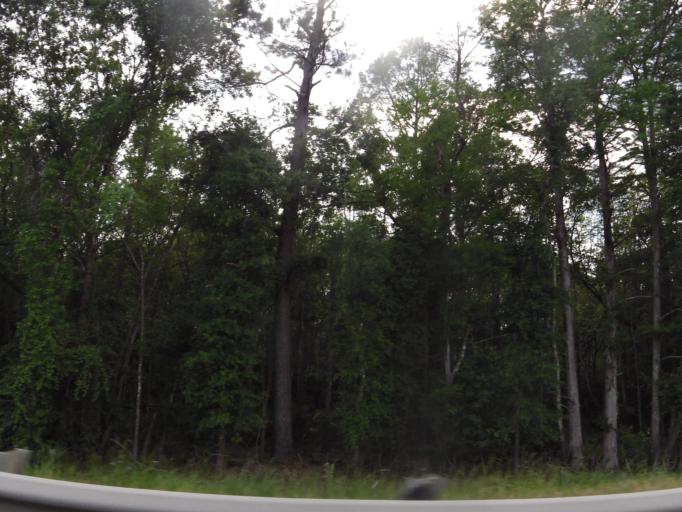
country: US
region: Georgia
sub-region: Charlton County
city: Folkston
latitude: 30.8032
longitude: -81.9919
